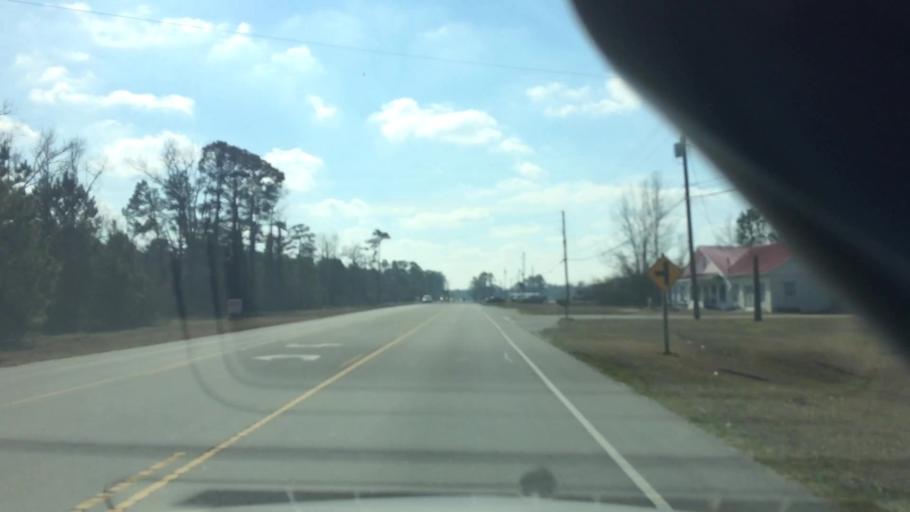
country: US
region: North Carolina
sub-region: Duplin County
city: Beulaville
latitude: 35.0745
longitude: -77.7348
